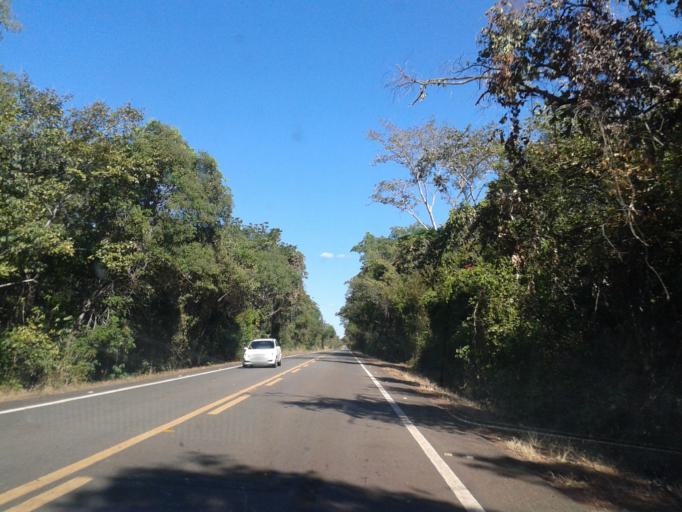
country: BR
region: Goias
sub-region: Sao Miguel Do Araguaia
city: Sao Miguel do Araguaia
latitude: -13.8153
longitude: -50.3428
